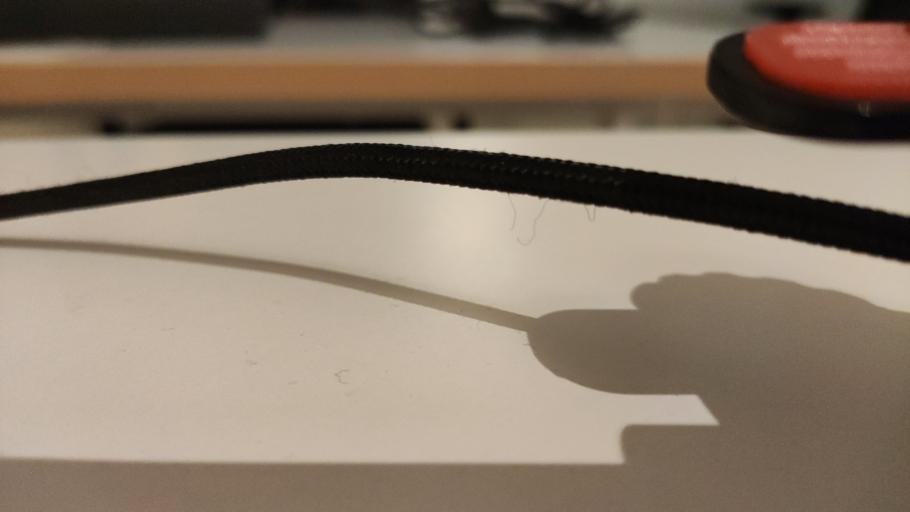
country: RU
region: Moskovskaya
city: Novoye
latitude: 55.6320
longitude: 38.9404
